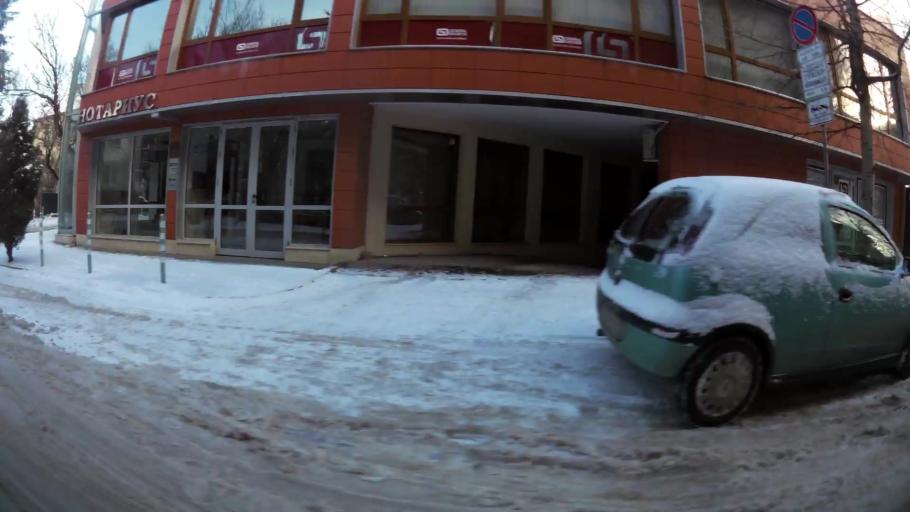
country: BG
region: Sofia-Capital
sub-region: Stolichna Obshtina
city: Sofia
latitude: 42.6726
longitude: 23.3292
